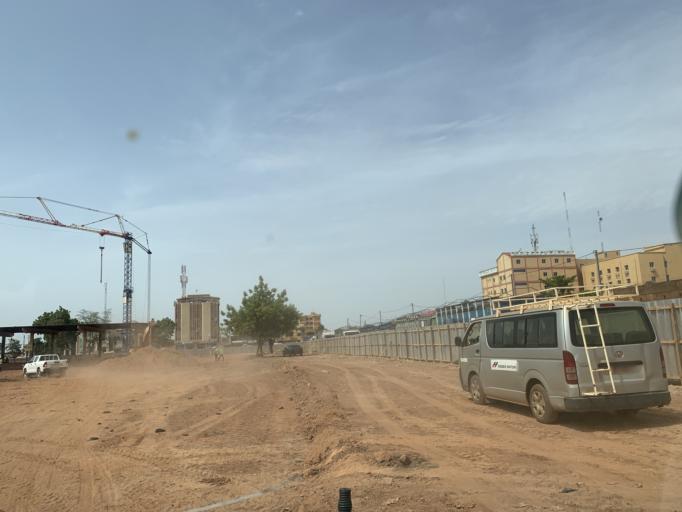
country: BF
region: Centre
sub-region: Kadiogo Province
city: Ouagadougou
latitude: 12.3345
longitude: -1.5167
